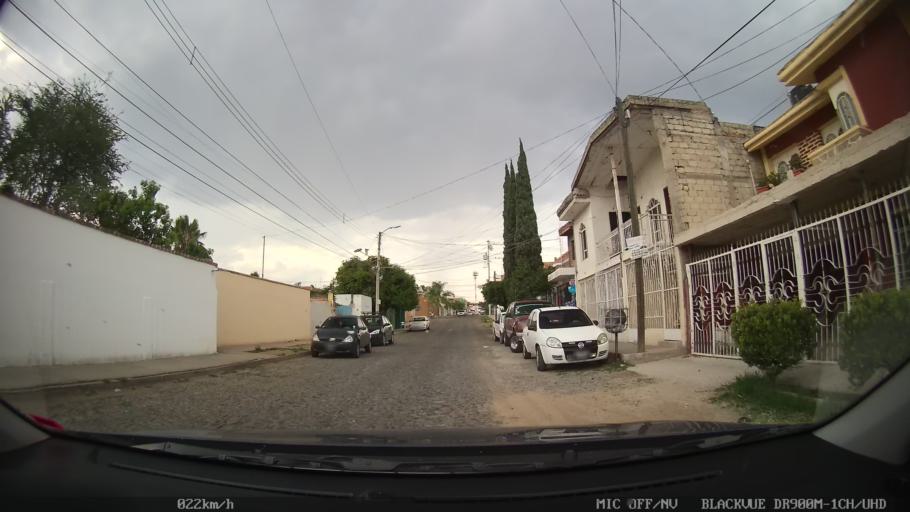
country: MX
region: Jalisco
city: Tlaquepaque
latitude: 20.6261
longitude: -103.2751
